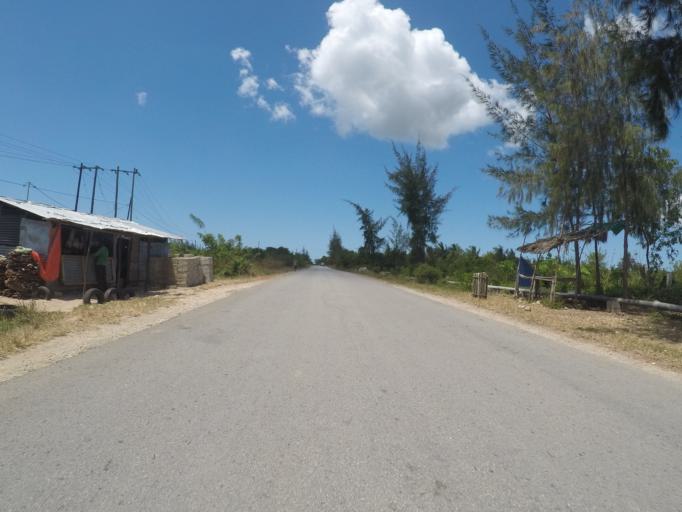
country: TZ
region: Zanzibar Central/South
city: Nganane
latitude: -6.2828
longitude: 39.4681
